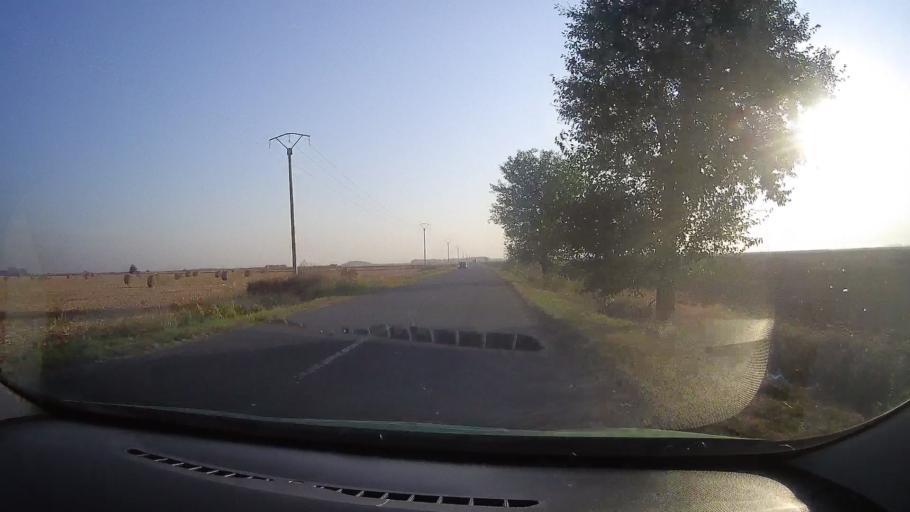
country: RO
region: Arad
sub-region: Comuna Curtici
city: Curtici
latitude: 46.3522
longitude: 21.3540
